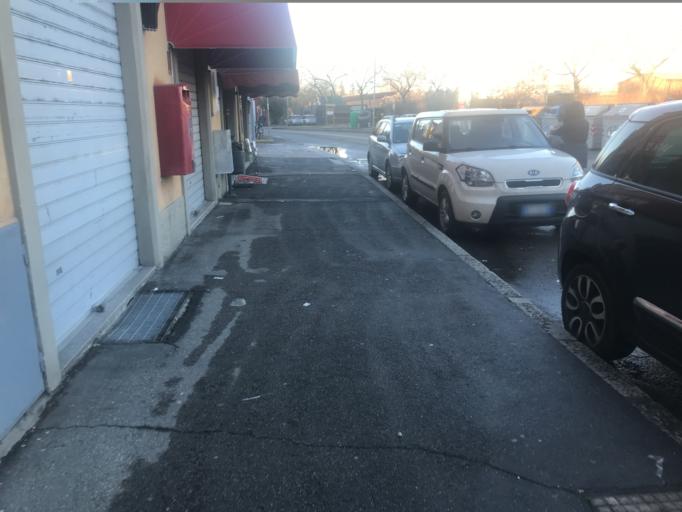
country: IT
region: Emilia-Romagna
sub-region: Provincia di Bologna
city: Progresso
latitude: 44.5387
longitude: 11.3517
